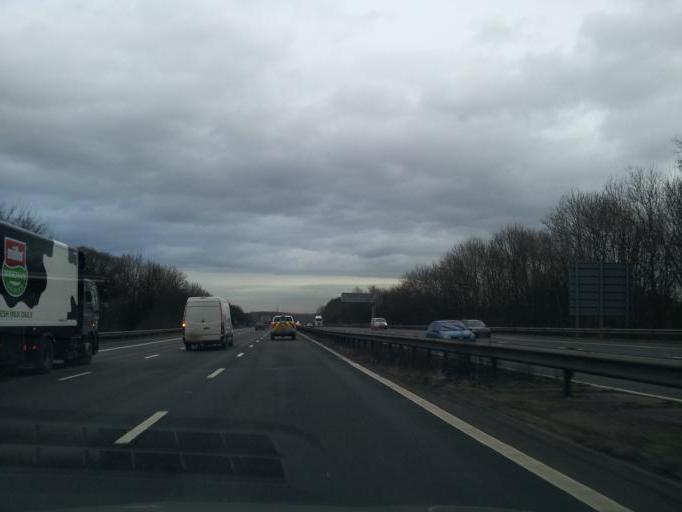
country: GB
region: England
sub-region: Coventry
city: Keresley
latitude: 52.4700
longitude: -1.5685
